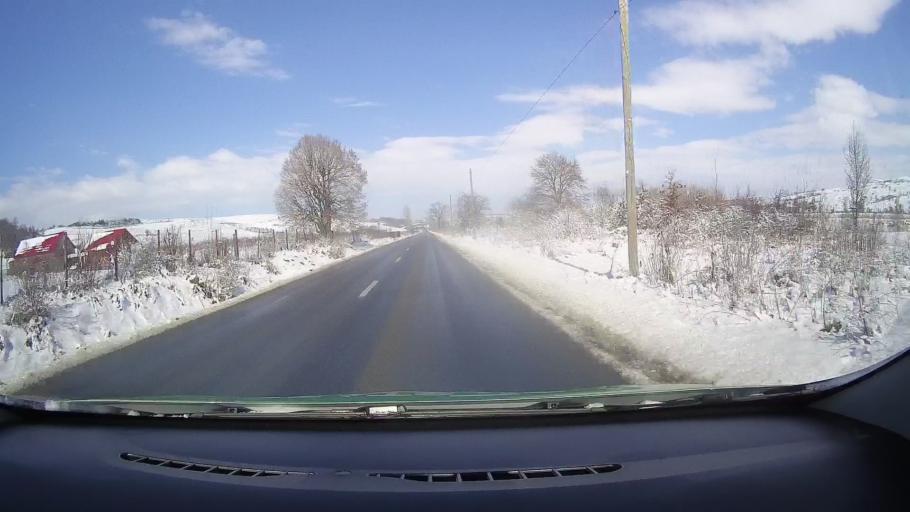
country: RO
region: Sibiu
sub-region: Comuna Nocrich
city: Nocrich
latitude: 45.8764
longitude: 24.4515
